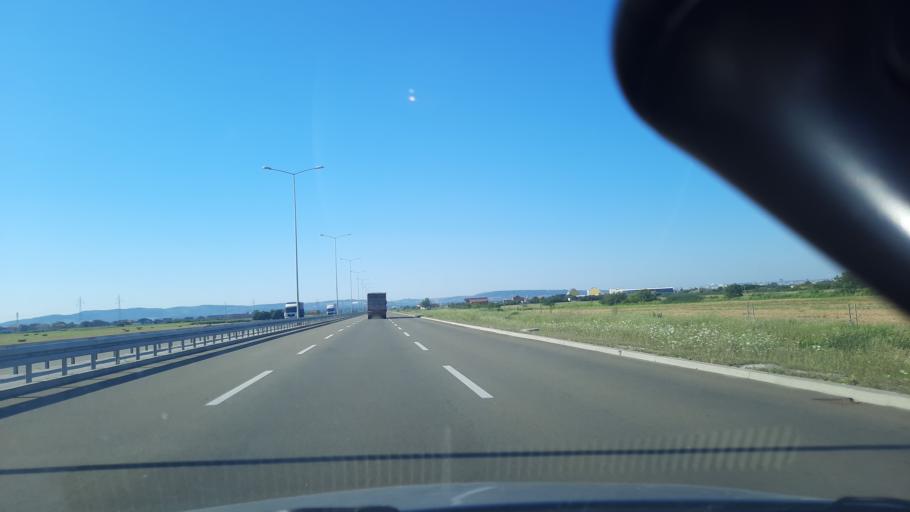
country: RS
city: Ovca
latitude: 44.8947
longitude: 20.5162
